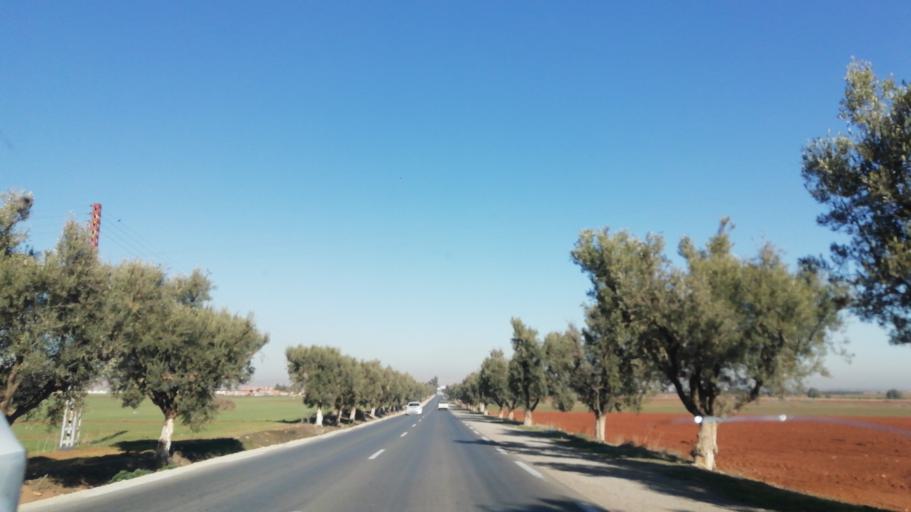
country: DZ
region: Mascara
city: Mascara
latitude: 35.2683
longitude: 0.1288
